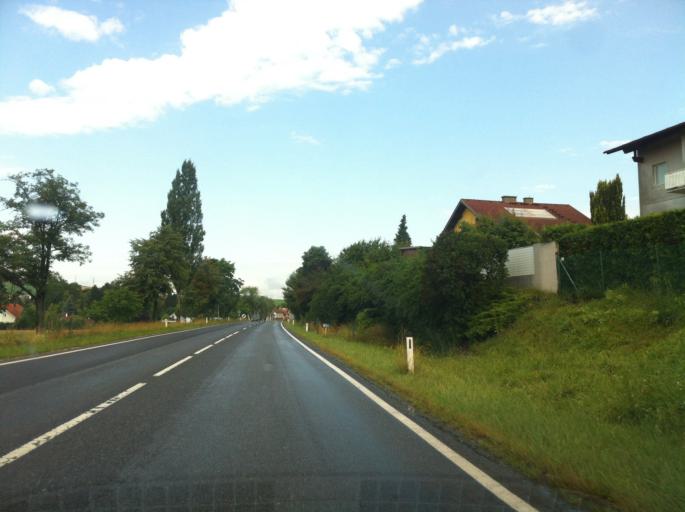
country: AT
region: Lower Austria
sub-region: Politischer Bezirk Tulln
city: Sieghartskirchen
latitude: 48.2531
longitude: 16.0230
